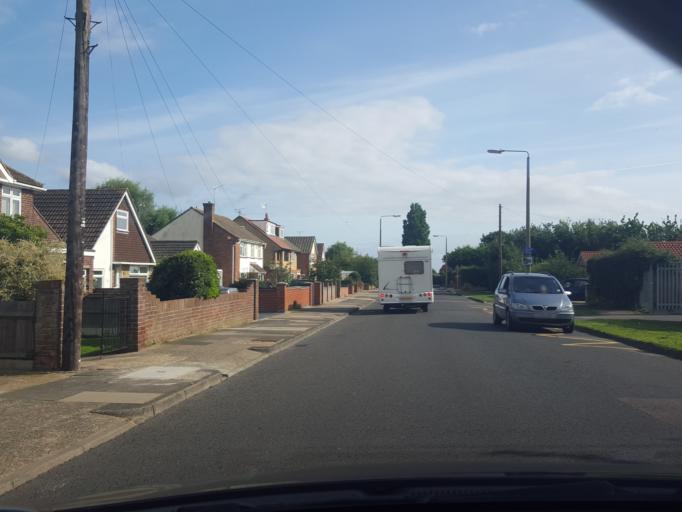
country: GB
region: England
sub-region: Essex
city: Dovercourt
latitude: 51.9285
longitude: 1.2634
